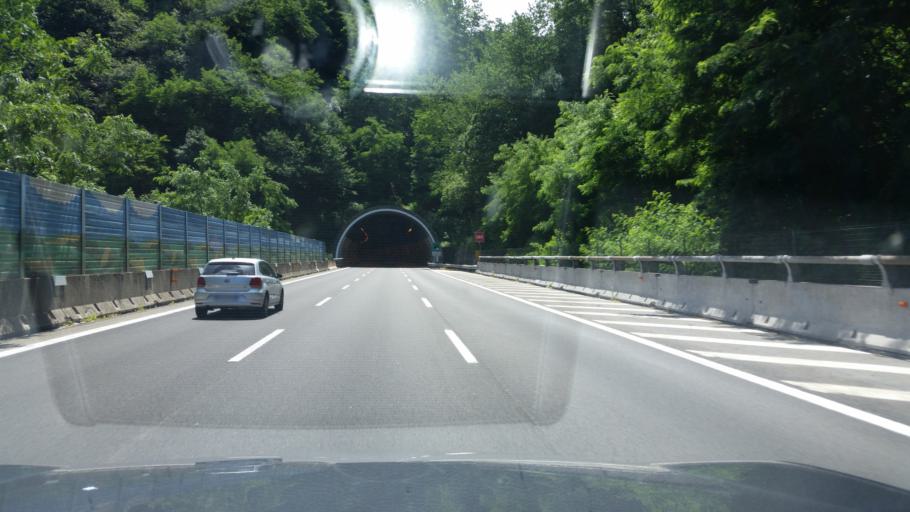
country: IT
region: Liguria
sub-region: Provincia di Genova
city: Rossiglione
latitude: 44.5668
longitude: 8.6617
